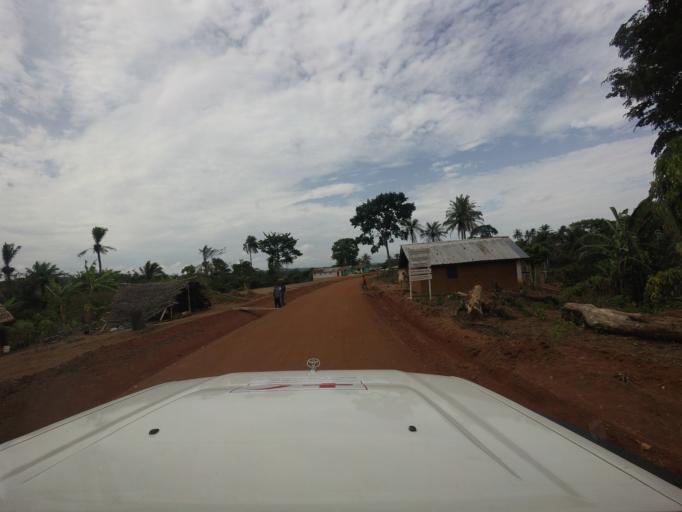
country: SL
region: Eastern Province
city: Buedu
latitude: 8.2149
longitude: -10.2238
